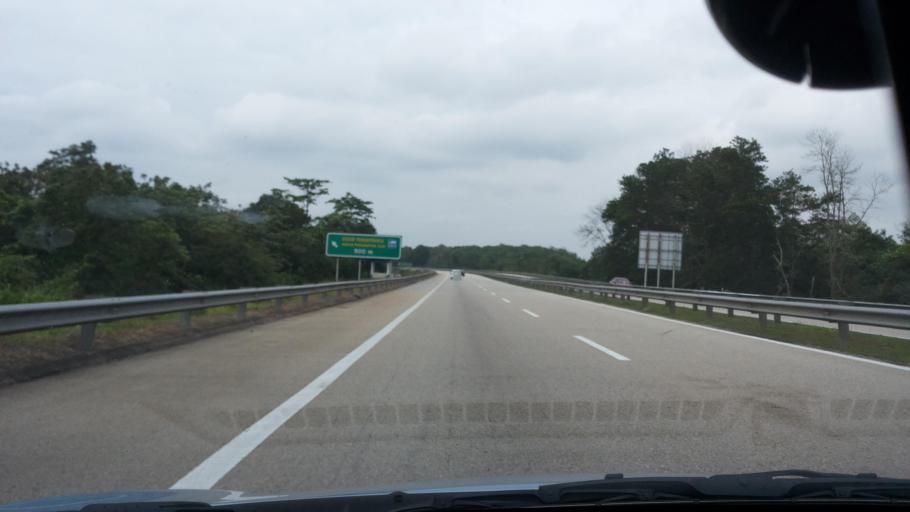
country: MY
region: Pahang
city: Kuantan
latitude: 3.8470
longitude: 103.2208
